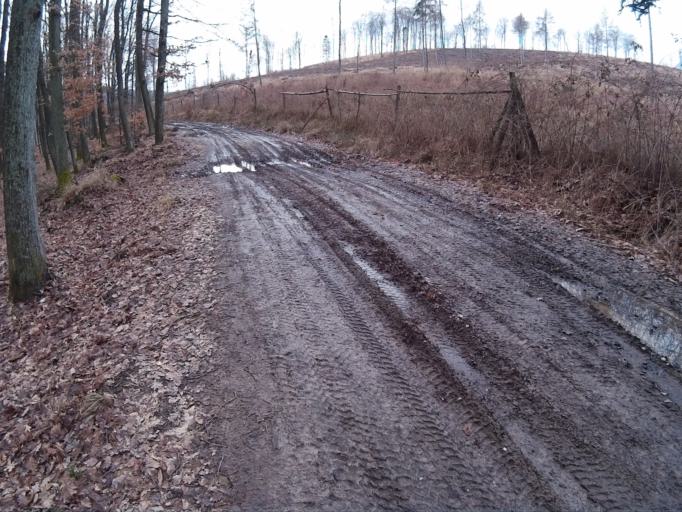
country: HU
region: Borsod-Abauj-Zemplen
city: Tolcsva
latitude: 48.4056
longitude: 21.4284
